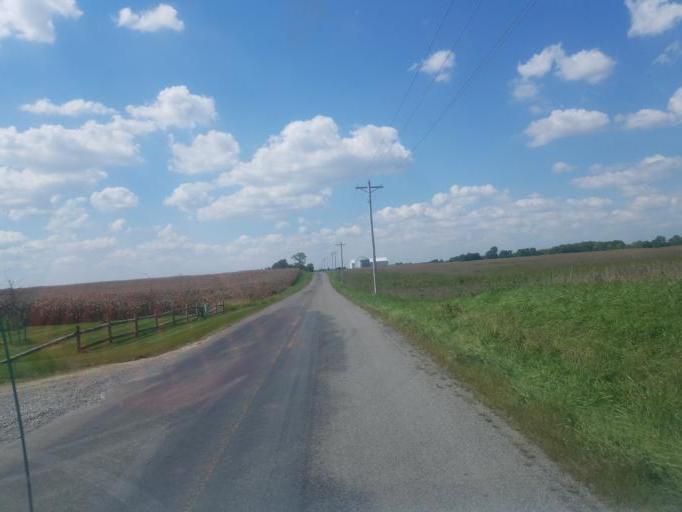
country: US
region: Ohio
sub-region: Hardin County
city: Ada
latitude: 40.6525
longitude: -83.8679
